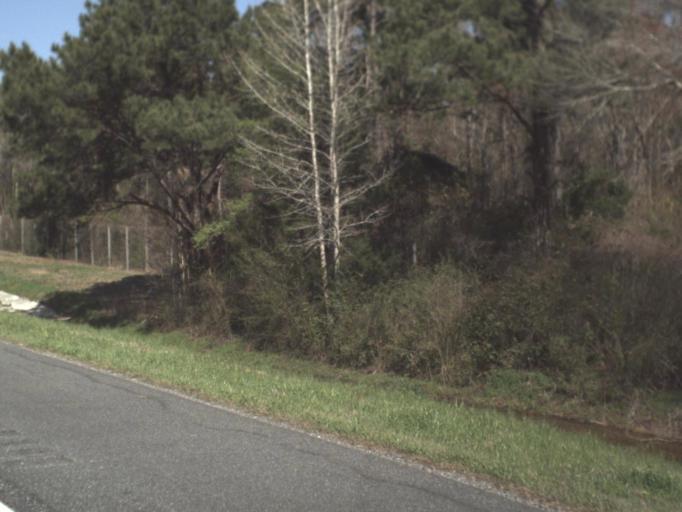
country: US
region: Florida
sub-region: Jackson County
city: Marianna
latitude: 30.7407
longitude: -85.2458
